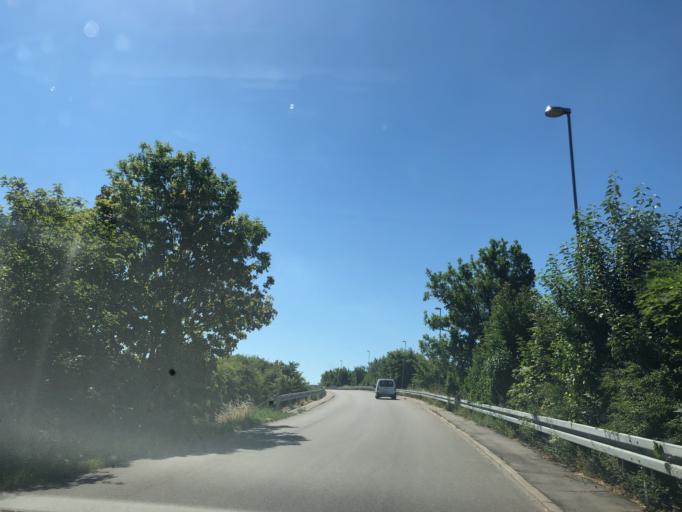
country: DK
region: Zealand
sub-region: Slagelse Kommune
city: Forlev
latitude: 55.3770
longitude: 11.2593
